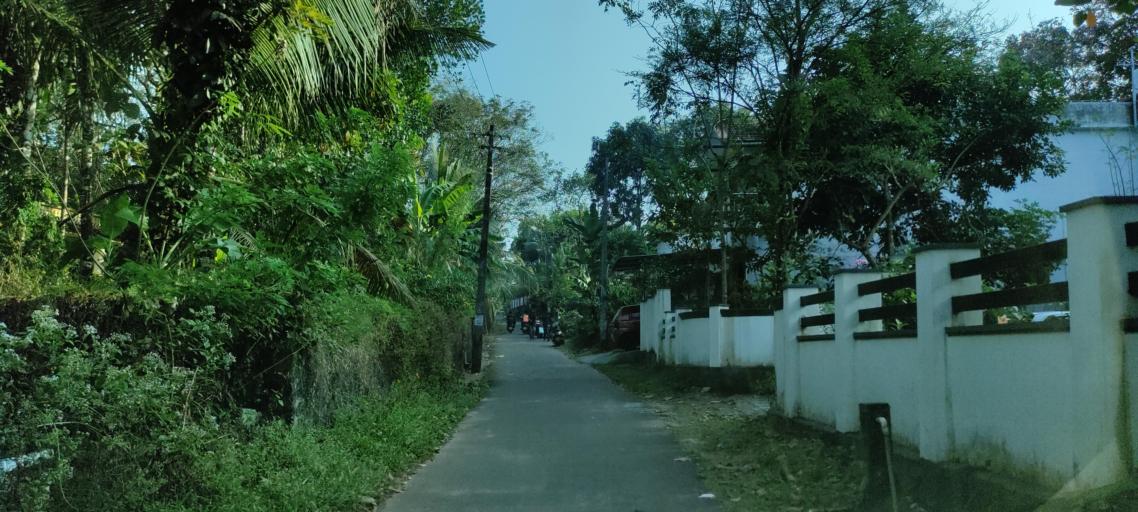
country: IN
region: Kerala
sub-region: Pattanamtitta
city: Adur
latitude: 9.1514
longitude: 76.7588
